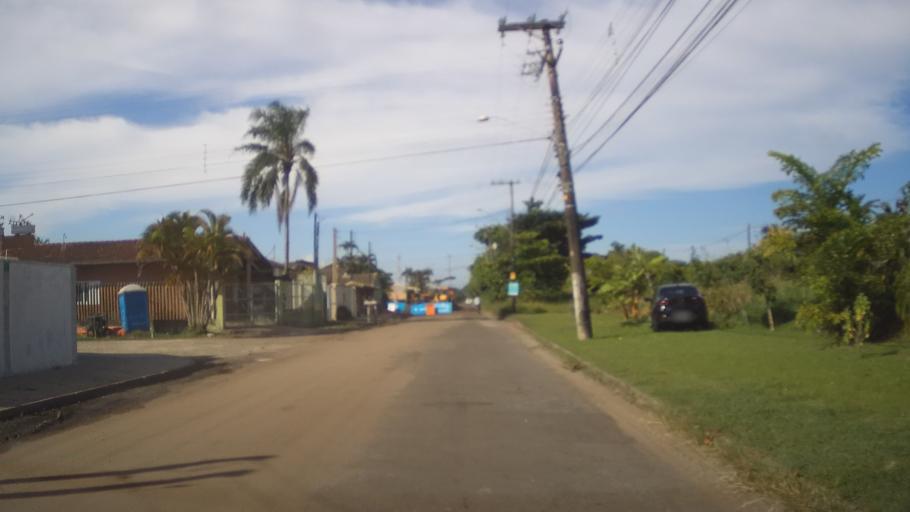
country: BR
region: Sao Paulo
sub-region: Itanhaem
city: Itanhaem
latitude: -24.2008
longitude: -46.8246
